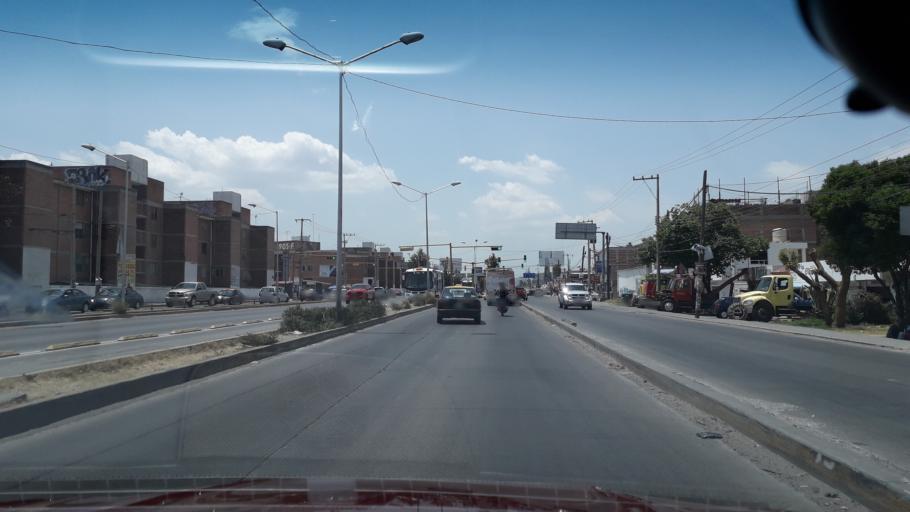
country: MX
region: Puebla
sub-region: Puebla
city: El Capulo (La Quebradora)
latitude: 18.9918
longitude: -98.2453
